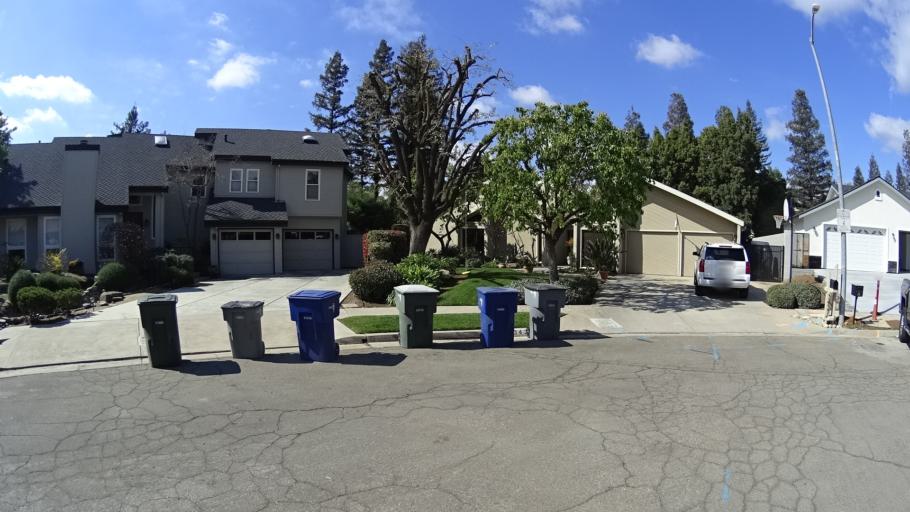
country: US
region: California
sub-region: Fresno County
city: Fresno
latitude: 36.8324
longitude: -119.8542
